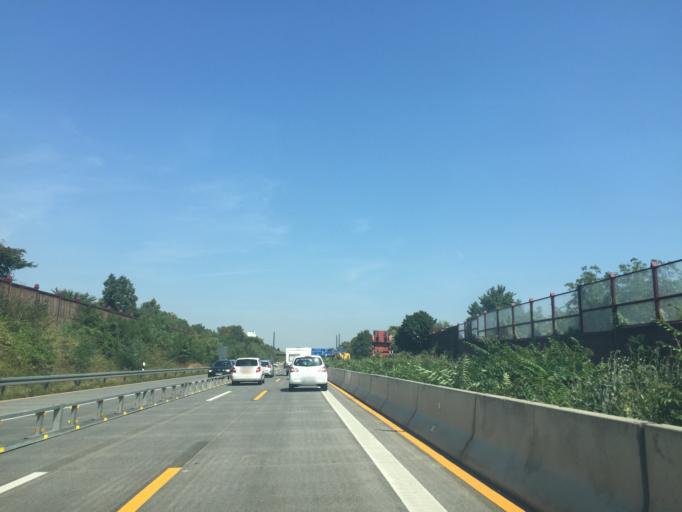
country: DE
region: Baden-Wuerttemberg
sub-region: Karlsruhe Region
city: Eppelheim
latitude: 49.3980
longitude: 8.6379
